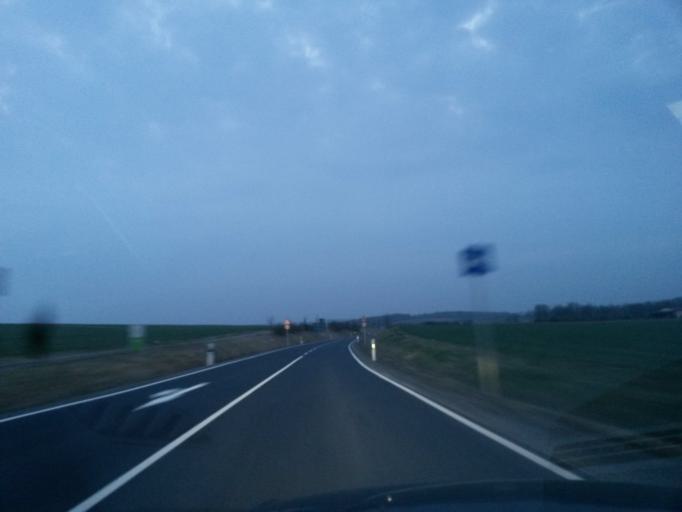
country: DE
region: Bavaria
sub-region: Regierungsbezirk Unterfranken
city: Rannungen
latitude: 50.2007
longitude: 10.2357
